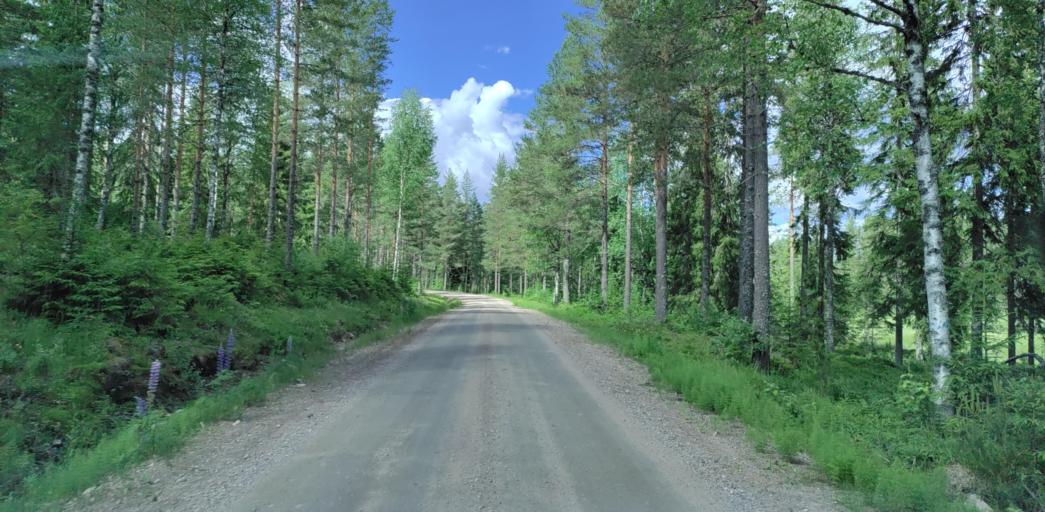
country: SE
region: Vaermland
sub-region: Hagfors Kommun
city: Ekshaerad
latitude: 60.1030
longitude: 13.3587
